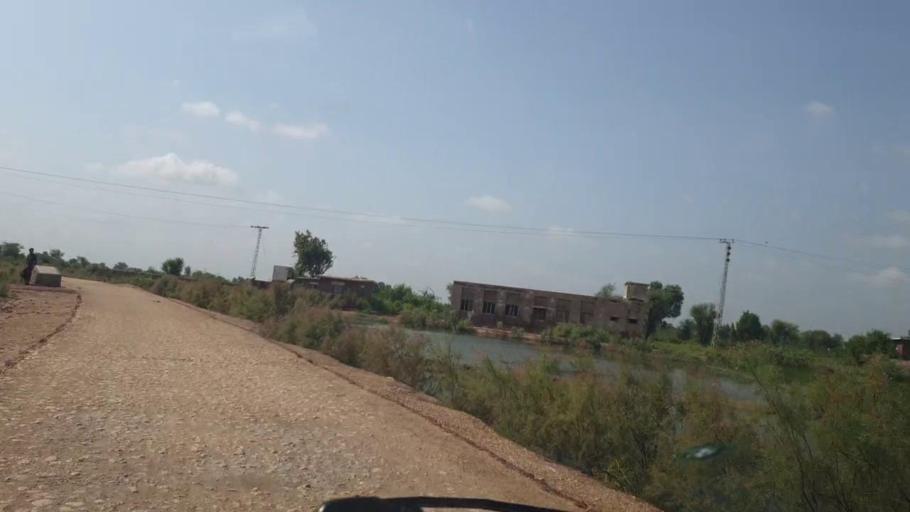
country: PK
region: Sindh
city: Berani
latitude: 25.7369
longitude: 68.9533
